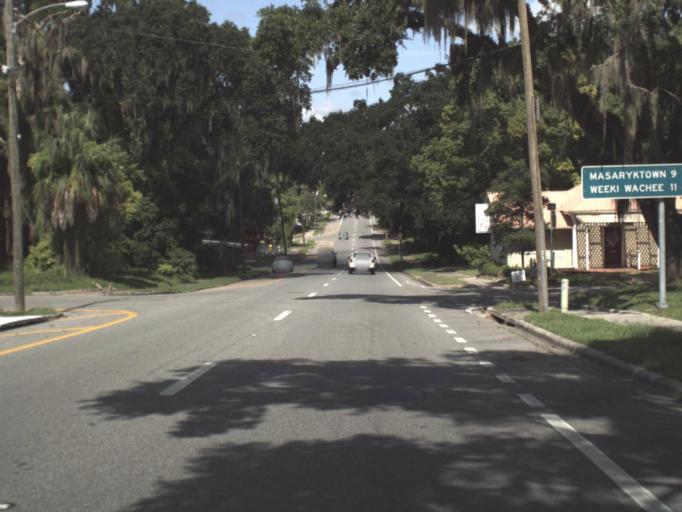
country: US
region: Florida
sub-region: Hernando County
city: Brooksville
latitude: 28.5557
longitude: -82.3819
